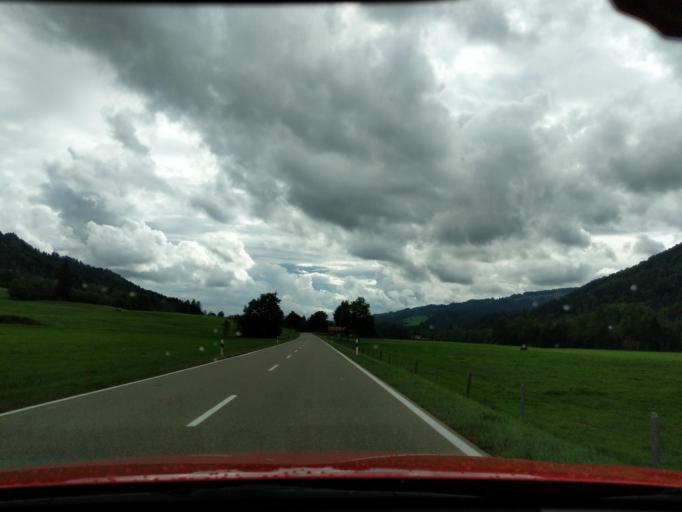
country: DE
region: Bavaria
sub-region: Swabia
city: Oberstaufen
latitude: 47.5362
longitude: 9.9992
